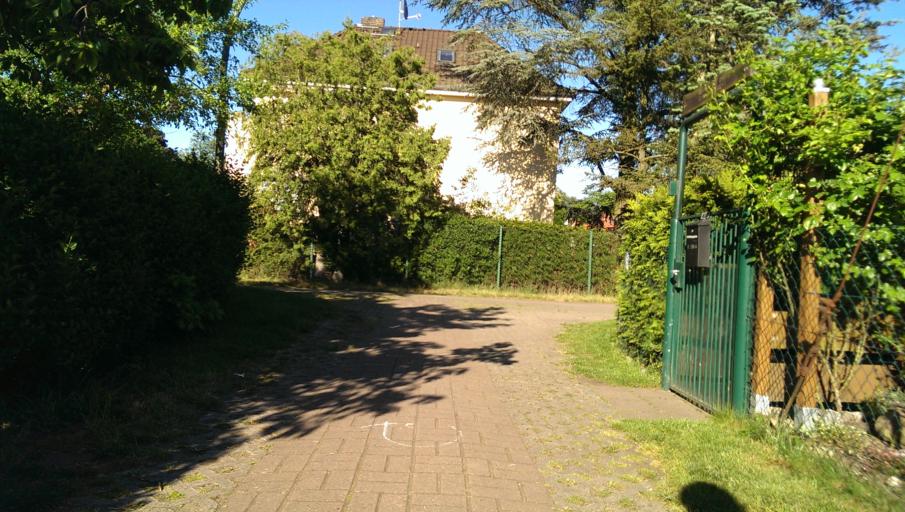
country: DE
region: Berlin
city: Lichterfelde
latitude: 52.4267
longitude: 13.2886
